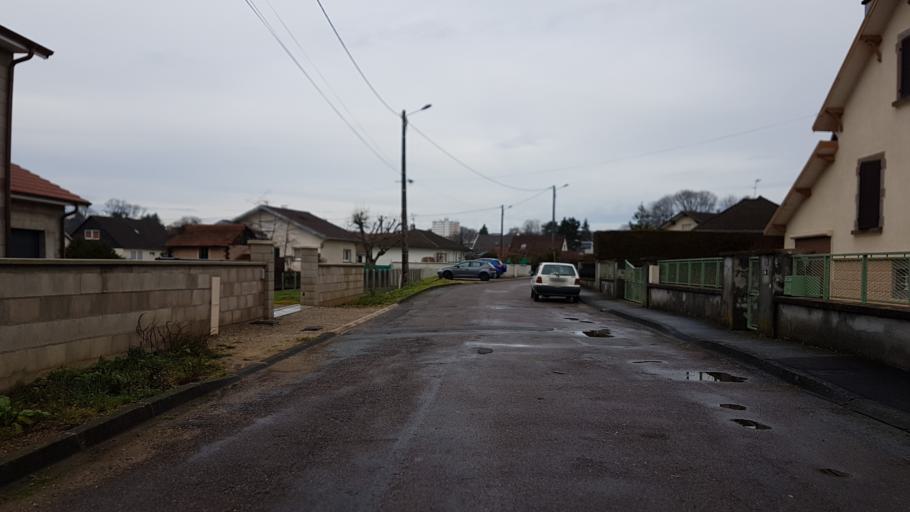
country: FR
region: Franche-Comte
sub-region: Departement de la Haute-Saone
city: Luxeuil-les-Bains
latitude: 47.8115
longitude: 6.3684
